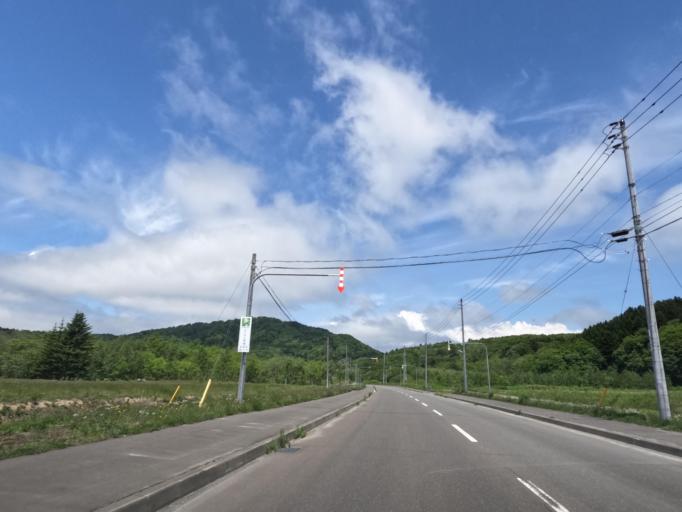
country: JP
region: Hokkaido
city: Tobetsu
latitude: 43.3097
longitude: 141.5572
